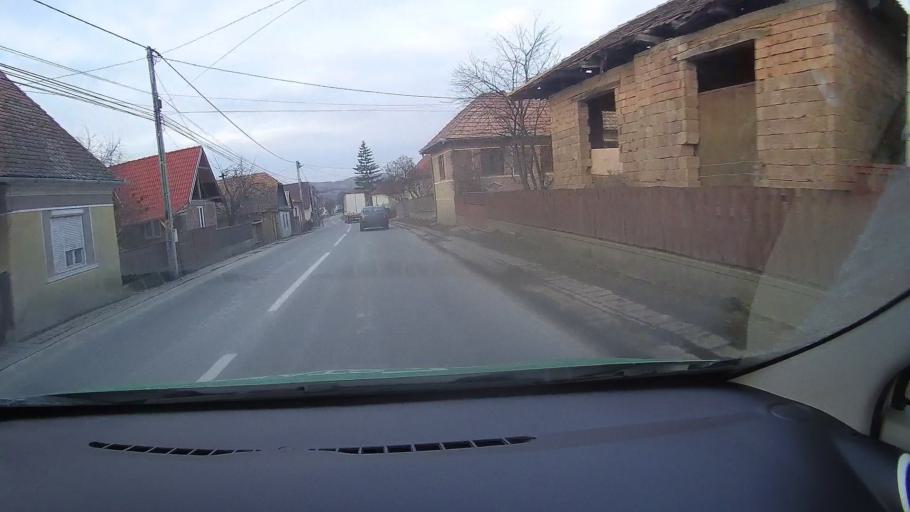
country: RO
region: Harghita
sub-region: Comuna Simonesti
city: Simonesti
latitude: 46.3329
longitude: 25.1065
